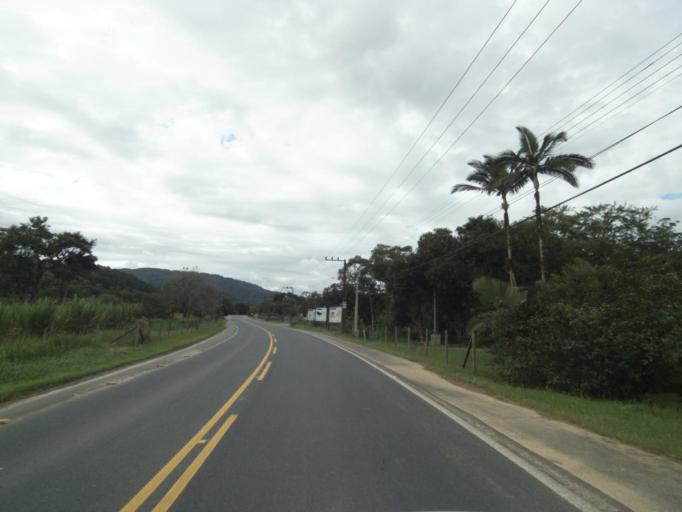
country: BR
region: Santa Catarina
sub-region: Pomerode
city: Pomerode
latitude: -26.7283
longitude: -49.2114
